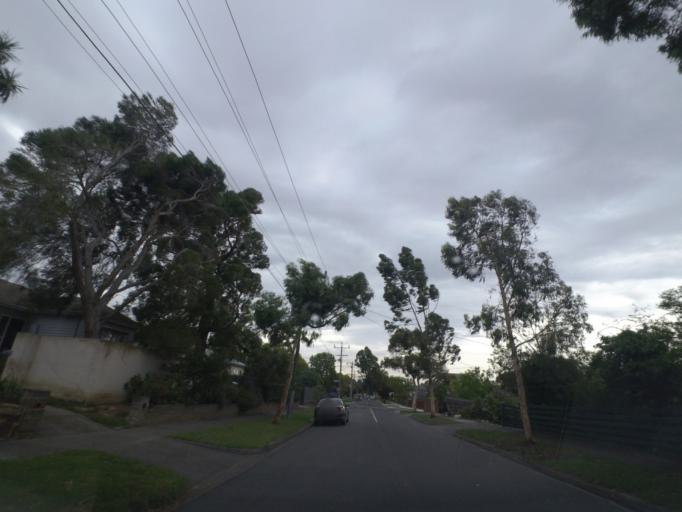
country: AU
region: Victoria
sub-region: Whitehorse
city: Box Hill North
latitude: -37.7998
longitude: 145.1245
